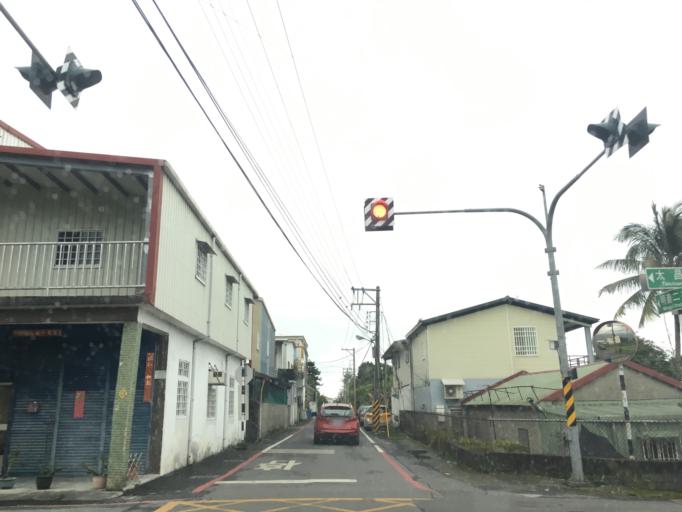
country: TW
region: Taiwan
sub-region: Hualien
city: Hualian
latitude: 23.9897
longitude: 121.5705
